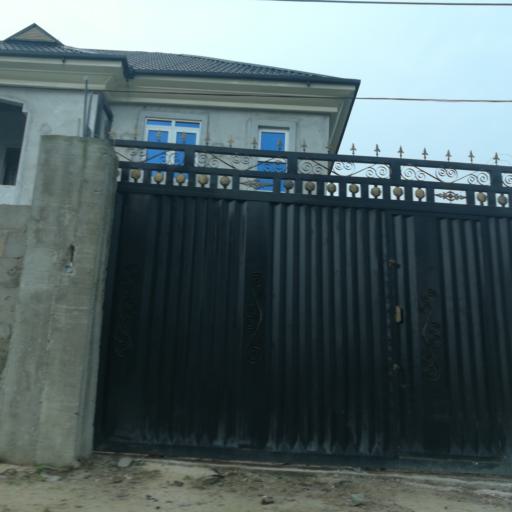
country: NG
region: Rivers
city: Port Harcourt
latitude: 4.7521
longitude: 7.0095
